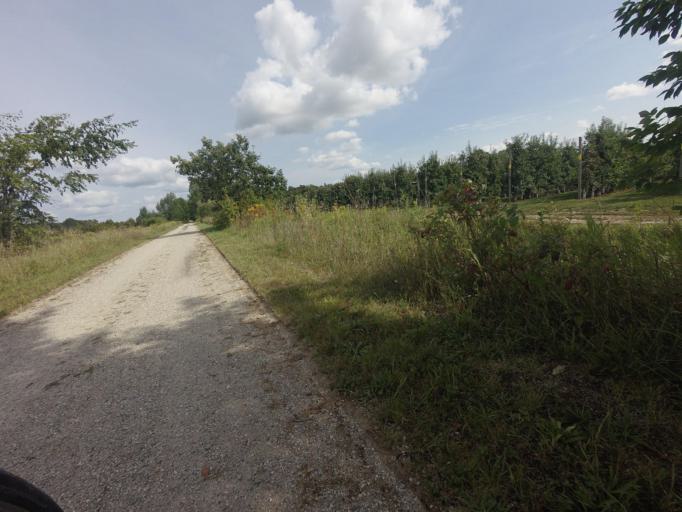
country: CA
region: Ontario
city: Waterloo
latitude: 43.5984
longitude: -80.5002
